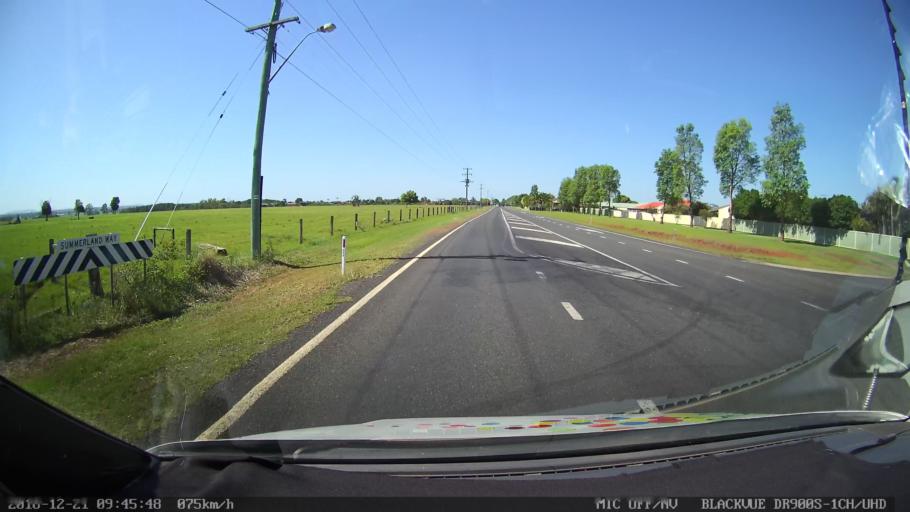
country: AU
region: New South Wales
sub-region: Clarence Valley
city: Grafton
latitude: -29.6330
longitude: 152.9278
